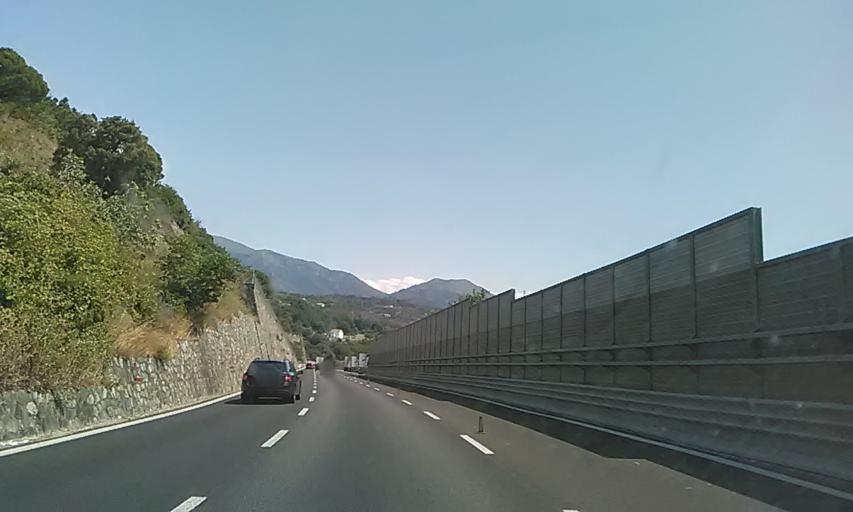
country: IT
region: Liguria
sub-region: Provincia di Genova
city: Cogoleto
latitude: 44.3840
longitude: 8.6338
